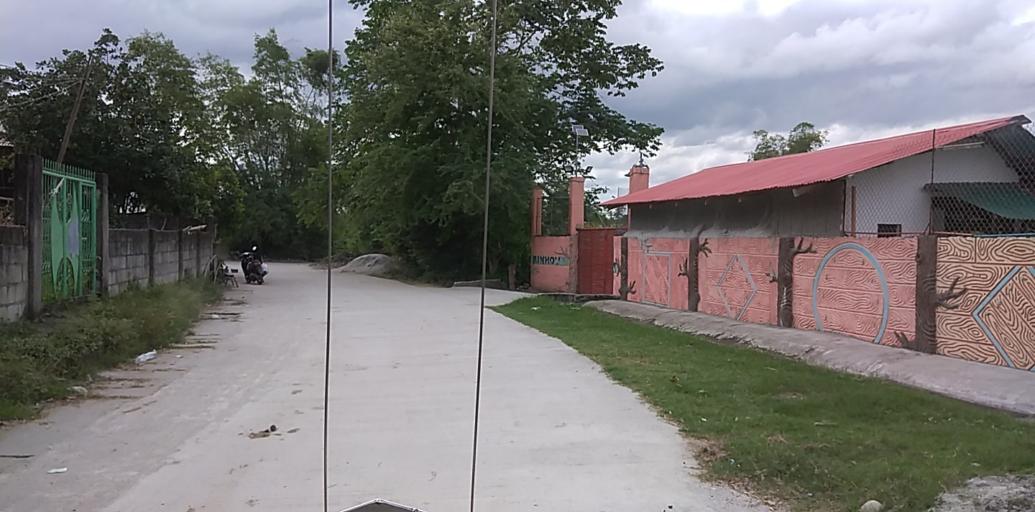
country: PH
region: Central Luzon
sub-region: Province of Pampanga
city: Porac
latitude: 15.0620
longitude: 120.5333
